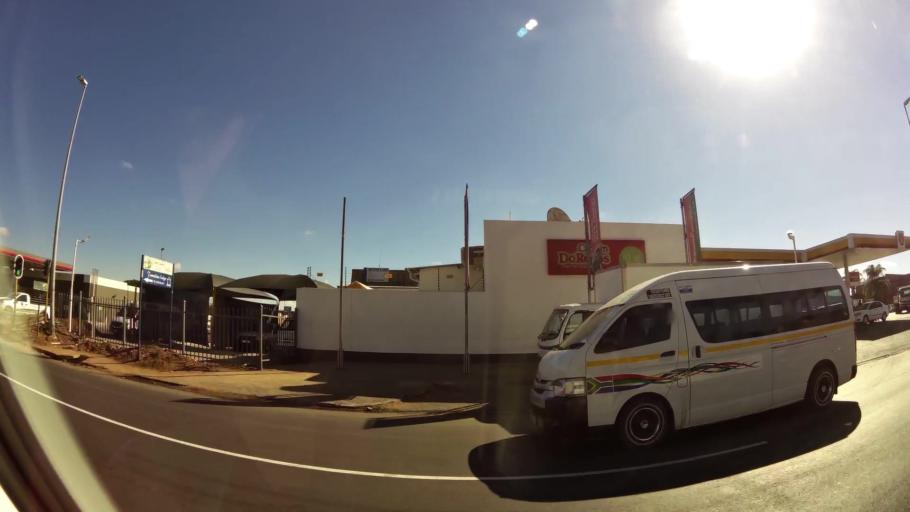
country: ZA
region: Limpopo
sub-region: Capricorn District Municipality
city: Polokwane
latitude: -23.9123
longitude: 29.4486
